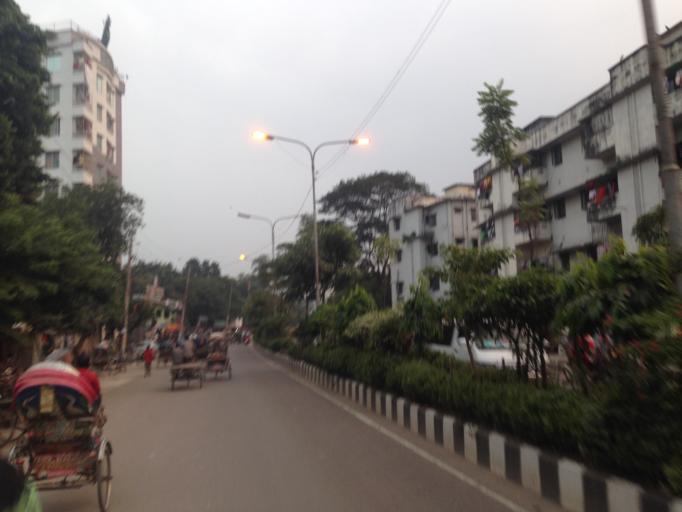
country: BD
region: Dhaka
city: Paltan
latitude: 23.7373
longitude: 90.4227
